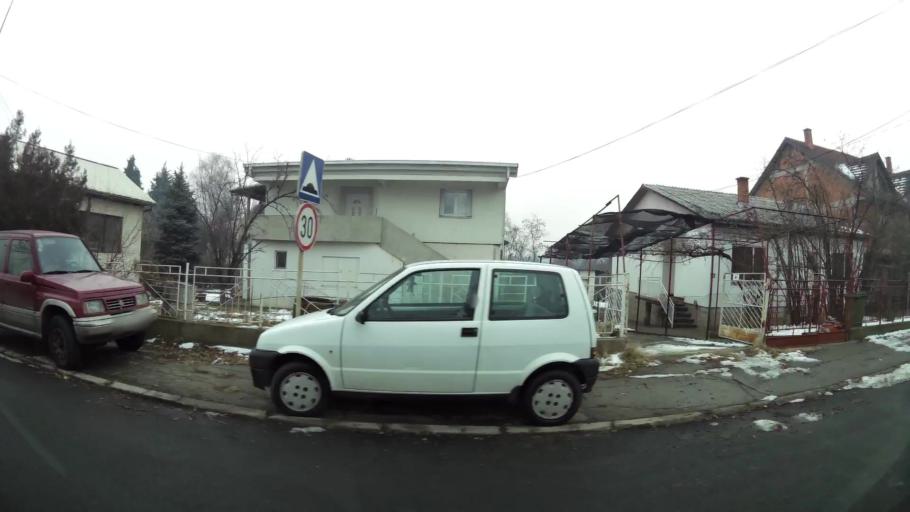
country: MK
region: Cair
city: Cair
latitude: 42.0138
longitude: 21.4604
